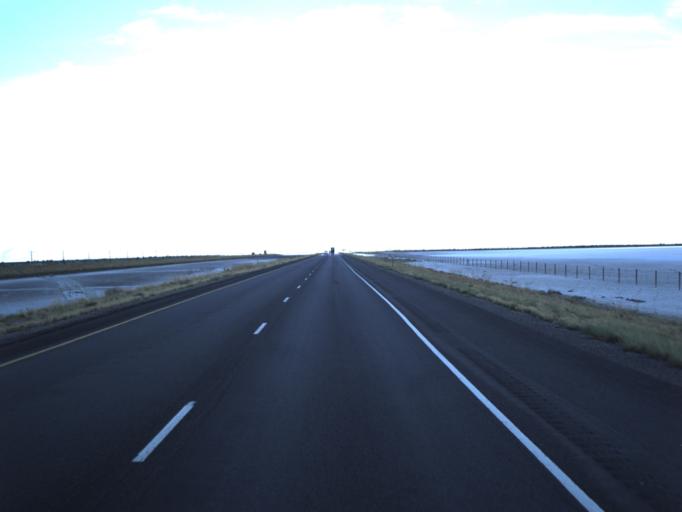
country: US
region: Utah
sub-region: Tooele County
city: Grantsville
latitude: 40.7259
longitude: -112.5754
